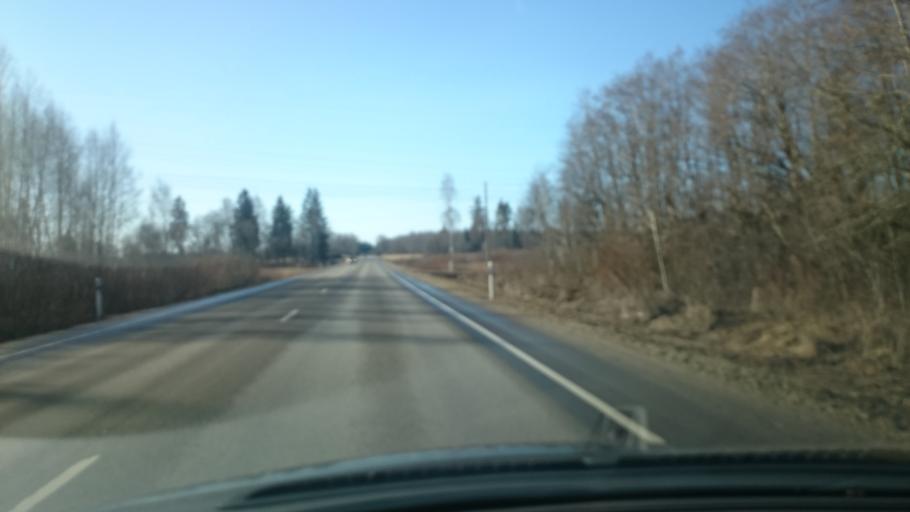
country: EE
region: Harju
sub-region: Saku vald
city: Saku
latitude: 59.2633
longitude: 24.7409
